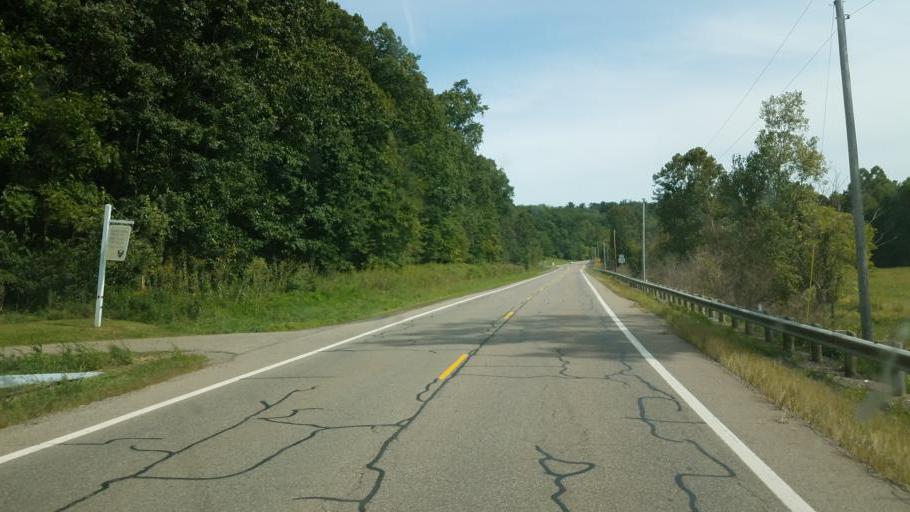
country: US
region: Ohio
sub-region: Knox County
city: Gambier
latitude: 40.3784
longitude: -82.4061
